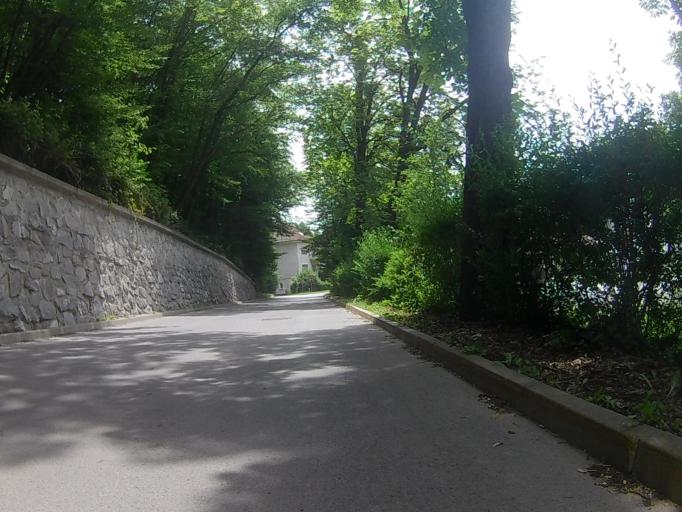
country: SI
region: Maribor
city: Maribor
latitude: 46.5701
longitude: 15.6481
